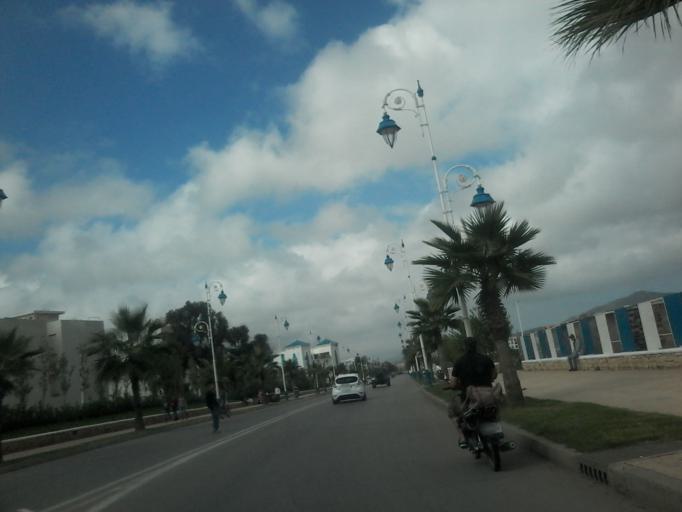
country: MA
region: Tanger-Tetouan
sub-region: Tetouan
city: Martil
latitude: 35.6280
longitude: -5.2821
